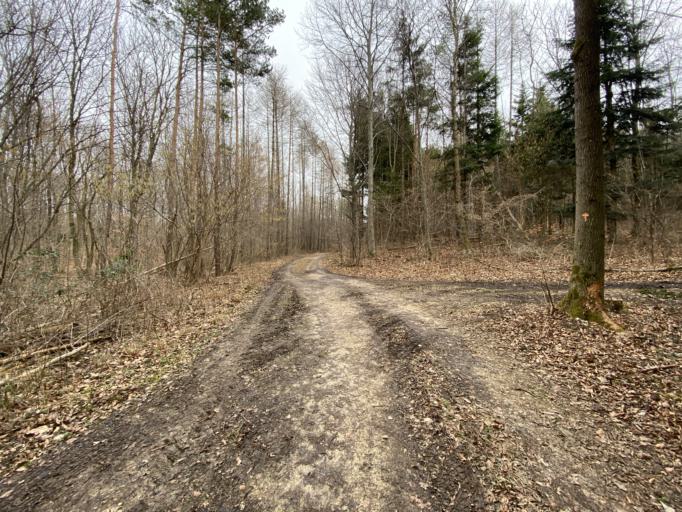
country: AT
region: Lower Austria
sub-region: Politischer Bezirk Baden
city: Baden
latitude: 48.0231
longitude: 16.2107
